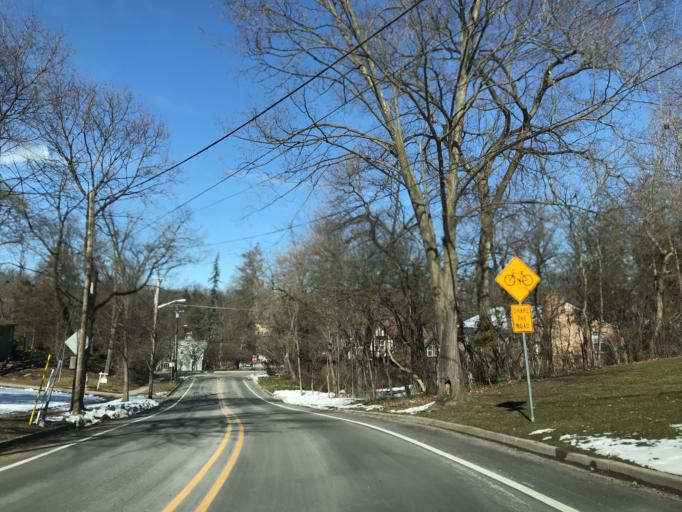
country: US
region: Michigan
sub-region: Washtenaw County
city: Ann Arbor
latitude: 42.2735
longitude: -83.7180
